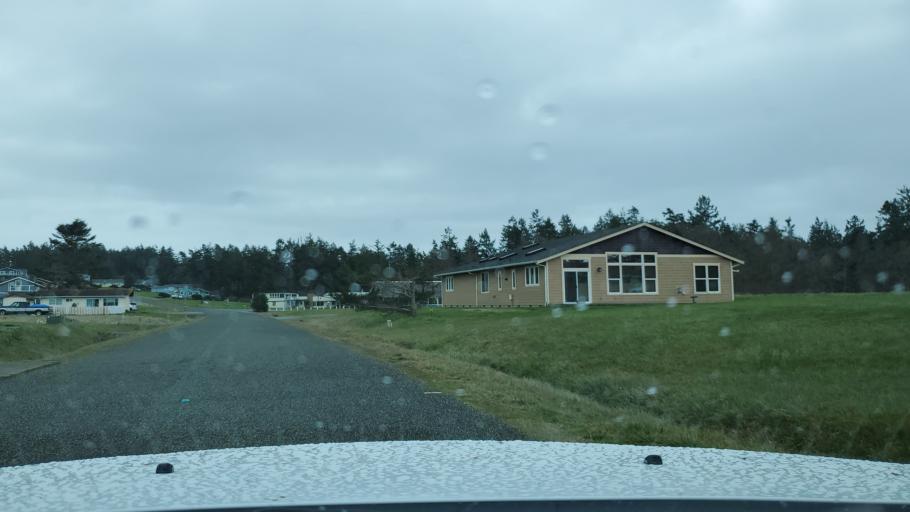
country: US
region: Washington
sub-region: Island County
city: Coupeville
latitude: 48.2340
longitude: -122.7638
